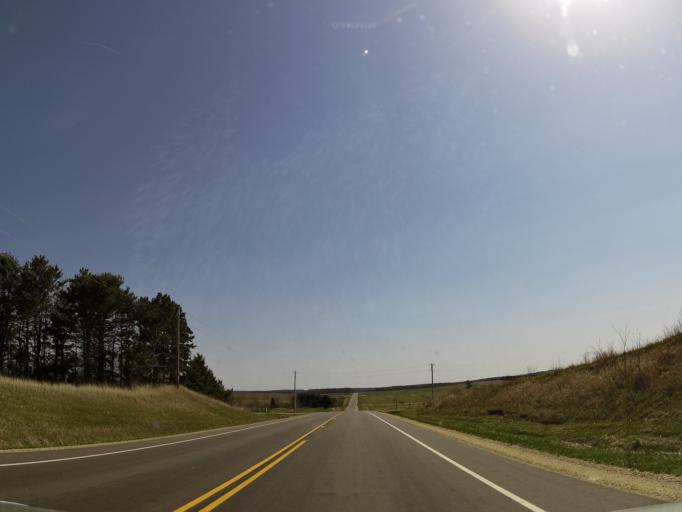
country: US
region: Wisconsin
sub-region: Saint Croix County
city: Hammond
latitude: 44.8961
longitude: -92.4355
